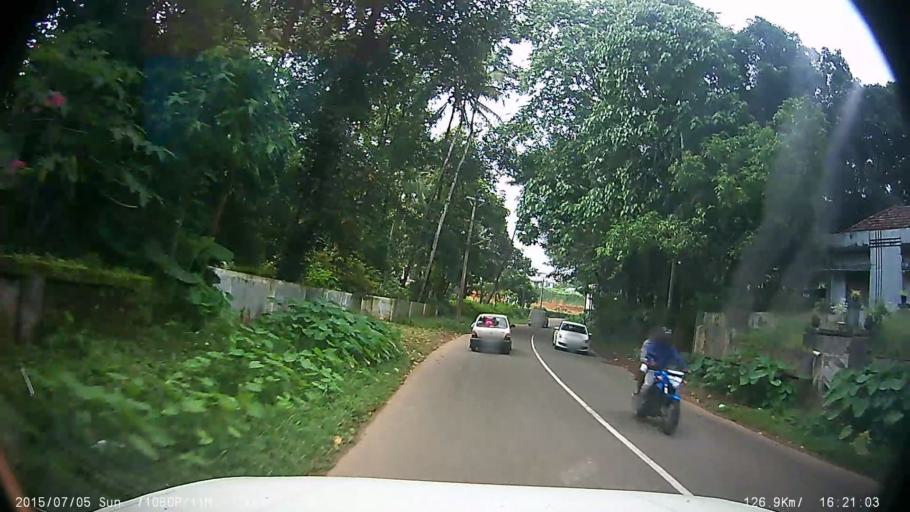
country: IN
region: Kerala
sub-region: Ernakulam
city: Muvattupuzha
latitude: 9.9510
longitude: 76.5763
